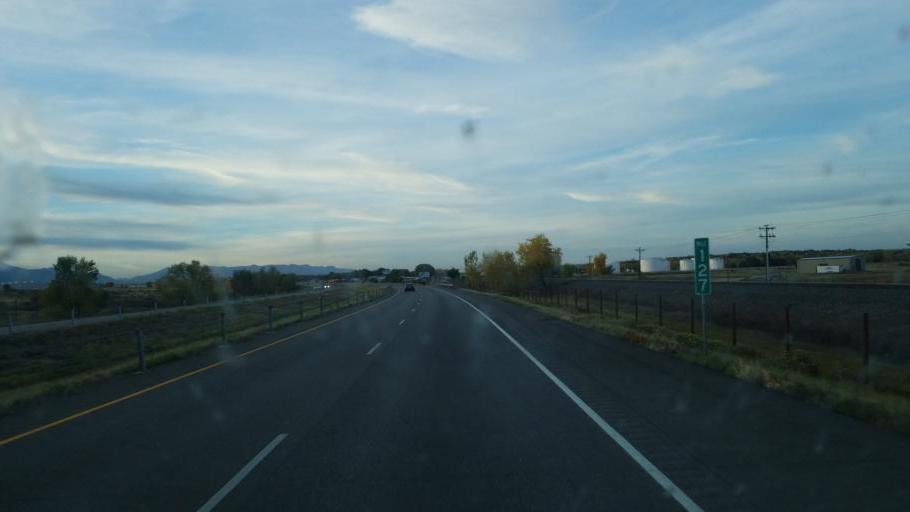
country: US
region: Colorado
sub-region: El Paso County
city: Fountain
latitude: 38.6614
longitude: -104.7006
